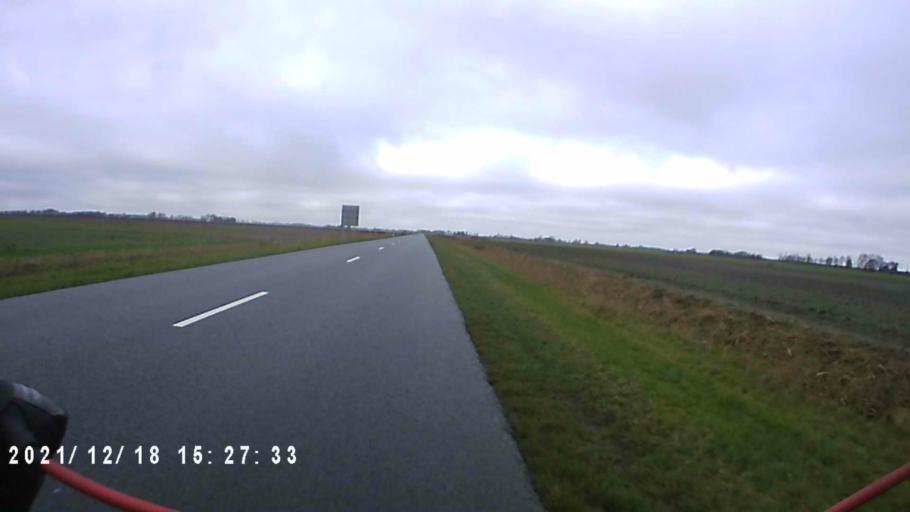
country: NL
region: Friesland
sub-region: Gemeente Dongeradeel
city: Anjum
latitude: 53.3298
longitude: 6.1468
